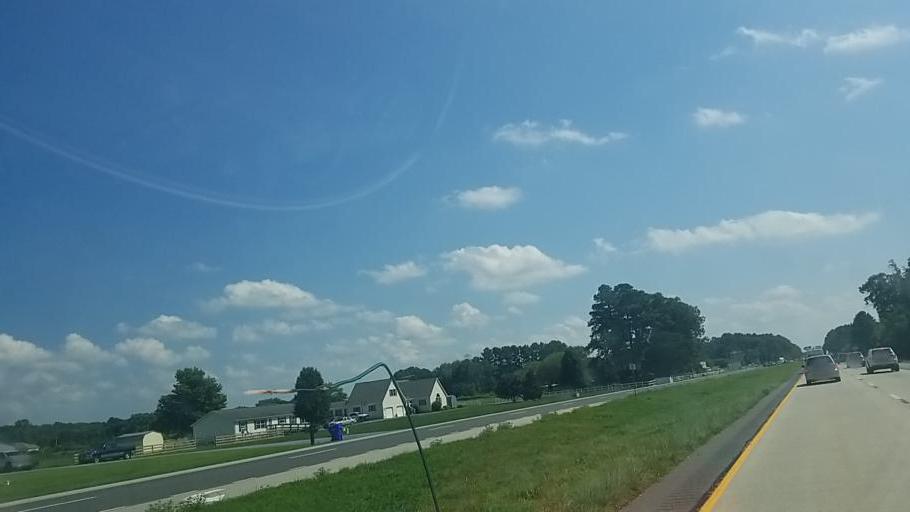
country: US
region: Delaware
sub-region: Sussex County
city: Milford
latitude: 38.8735
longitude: -75.4395
